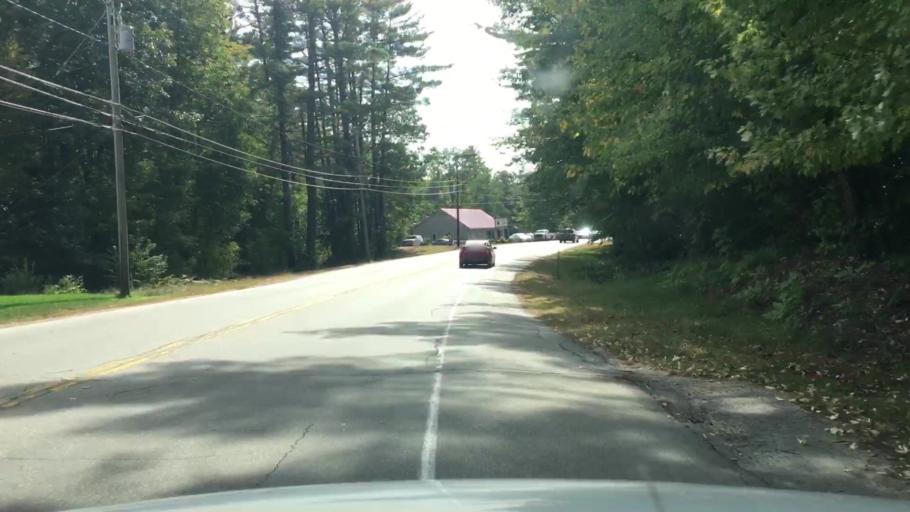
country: US
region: New Hampshire
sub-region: Carroll County
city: Conway
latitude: 43.9974
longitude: -71.1099
